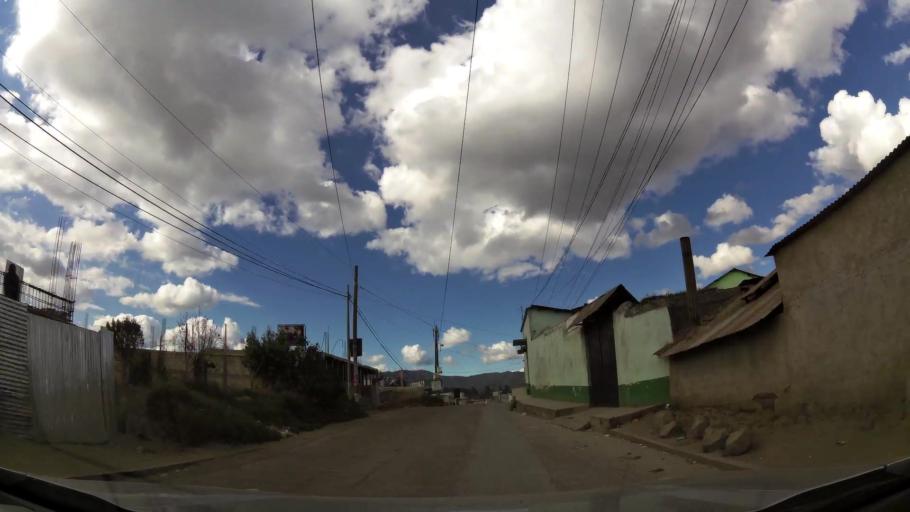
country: GT
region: Quetzaltenango
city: Quetzaltenango
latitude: 14.8327
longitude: -91.5357
